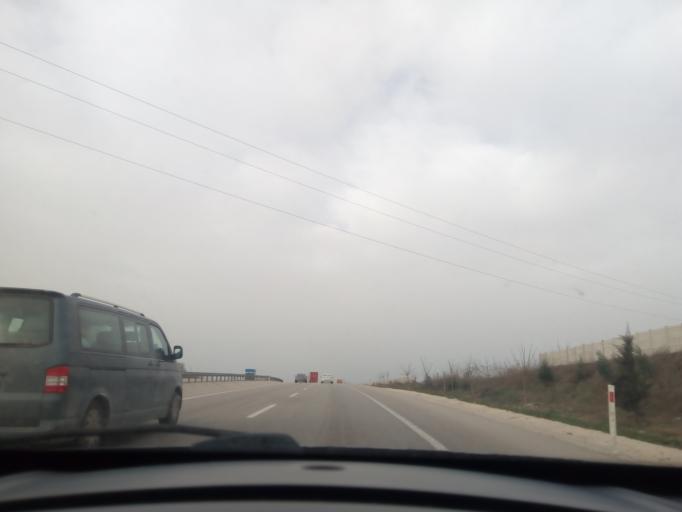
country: TR
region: Bursa
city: Mahmudiye
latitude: 40.2181
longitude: 28.6391
